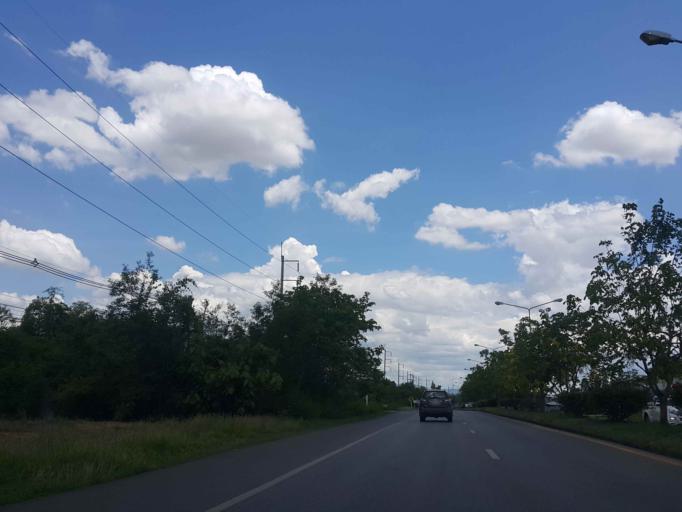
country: TH
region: Phrae
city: Nong Muang Khai
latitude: 18.2142
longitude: 100.1987
